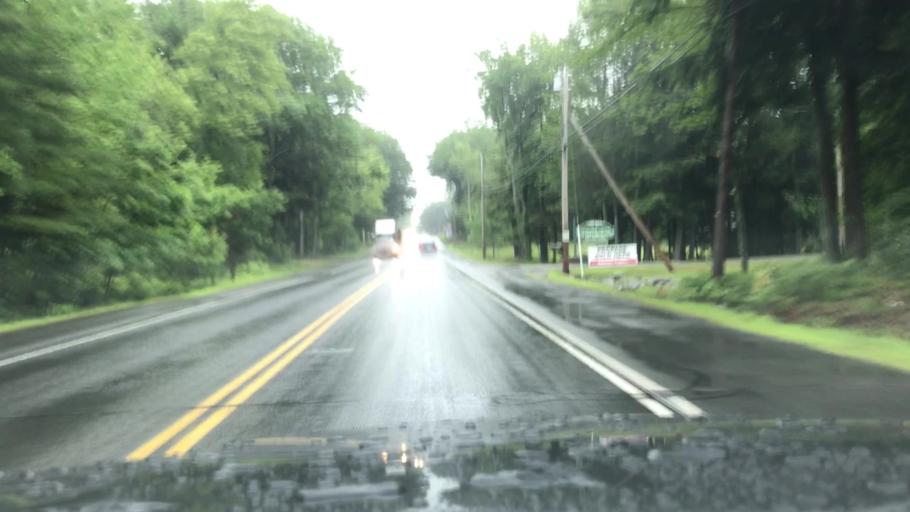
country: US
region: Maine
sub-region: York County
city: Kennebunk
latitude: 43.4123
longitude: -70.5205
